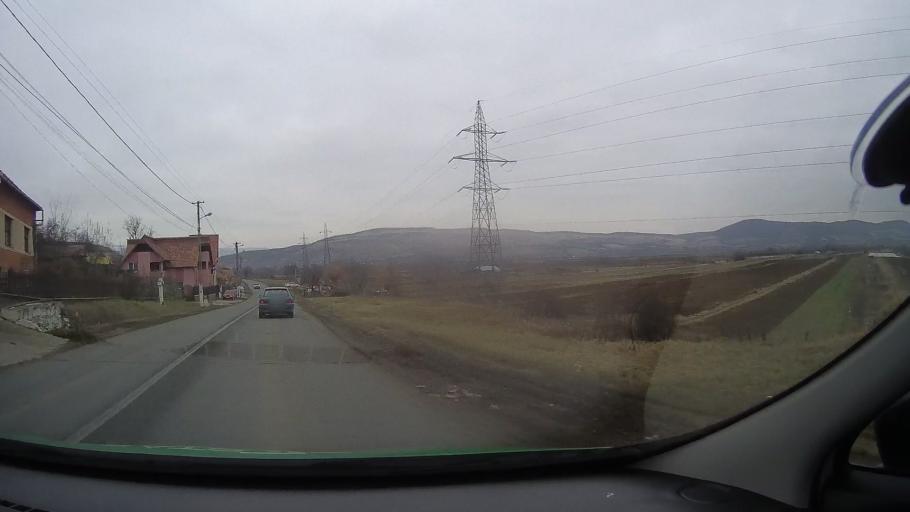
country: RO
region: Alba
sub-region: Comuna Ighiu
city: Sard
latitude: 46.1167
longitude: 23.5384
